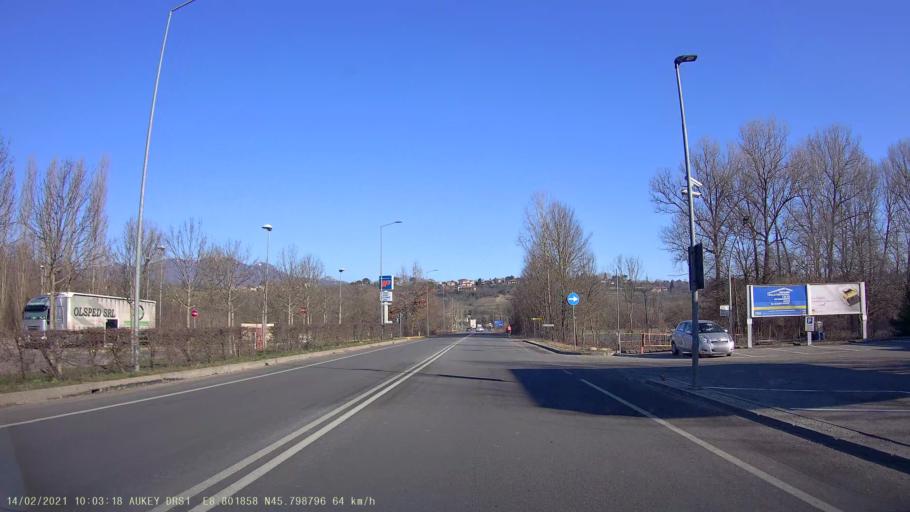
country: IT
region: Lombardy
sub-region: Provincia di Varese
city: Buguggiate
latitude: 45.7991
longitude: 8.8019
